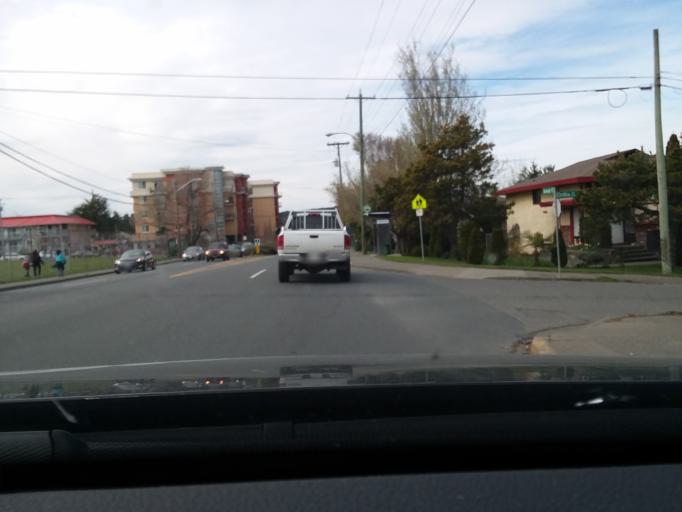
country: CA
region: British Columbia
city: Victoria
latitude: 48.4528
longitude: -123.3911
